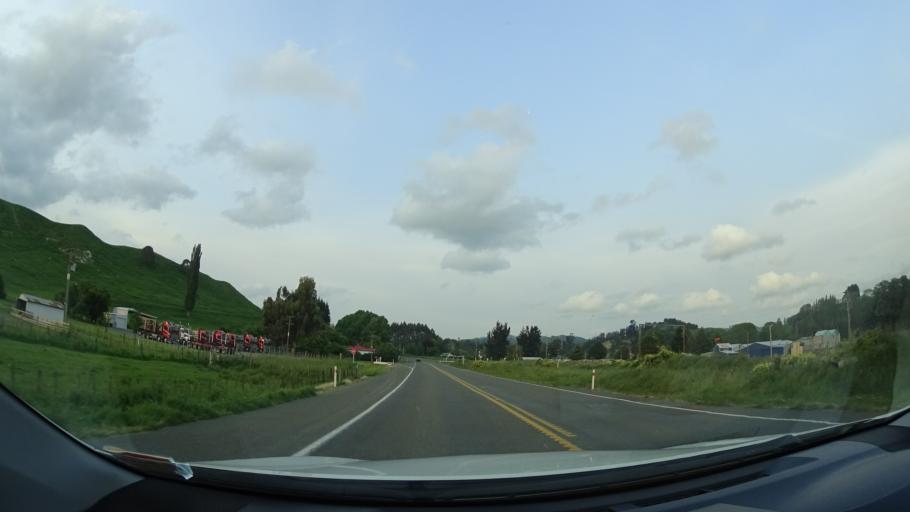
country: NZ
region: Manawatu-Wanganui
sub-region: Ruapehu District
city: Waiouru
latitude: -39.7349
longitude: 175.8427
